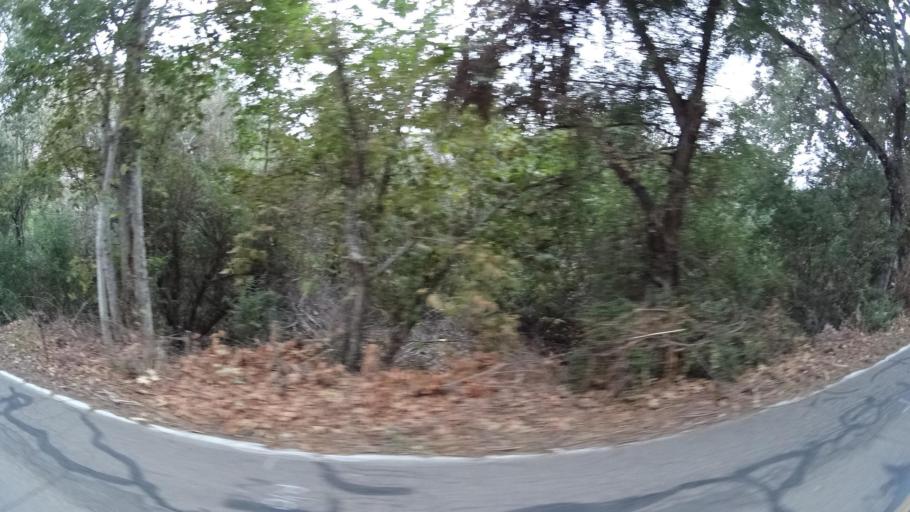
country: US
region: California
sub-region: San Diego County
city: Harbison Canyon
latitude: 32.8846
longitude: -116.8232
